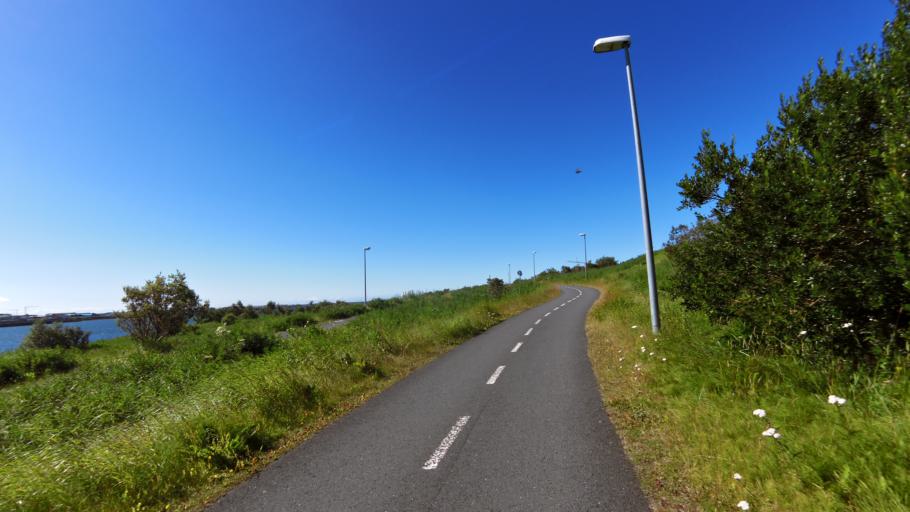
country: IS
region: Capital Region
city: Kopavogur
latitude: 64.1211
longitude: -21.9147
